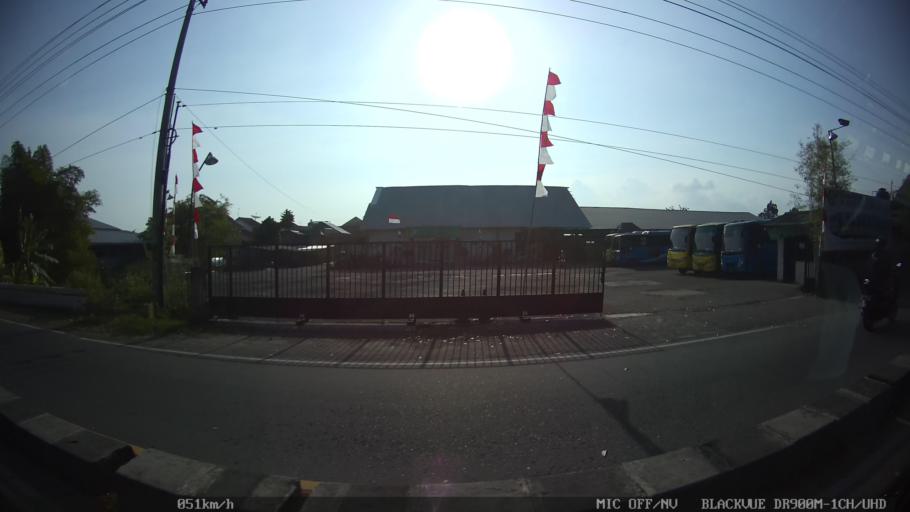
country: ID
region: Daerah Istimewa Yogyakarta
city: Sewon
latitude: -7.8316
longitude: 110.4071
